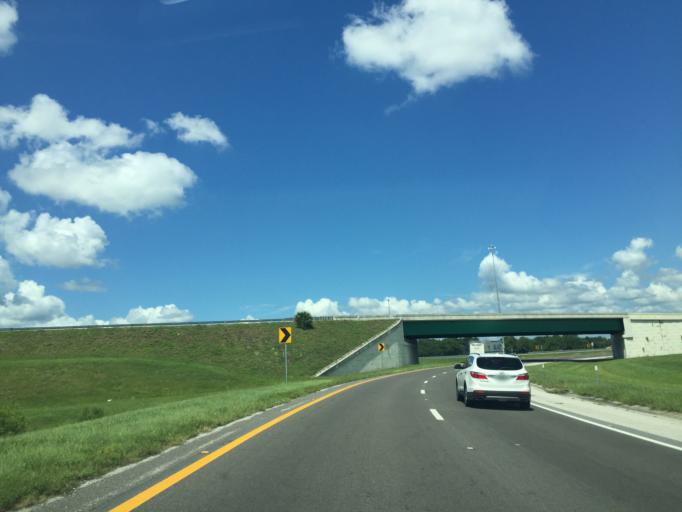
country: US
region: Florida
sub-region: Seminole County
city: Heathrow
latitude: 28.7975
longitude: -81.3426
